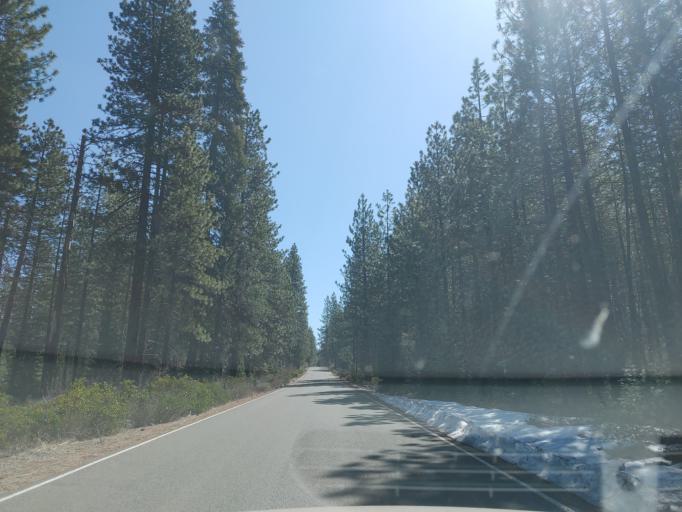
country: US
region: California
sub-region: Siskiyou County
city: McCloud
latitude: 41.2472
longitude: -122.0220
